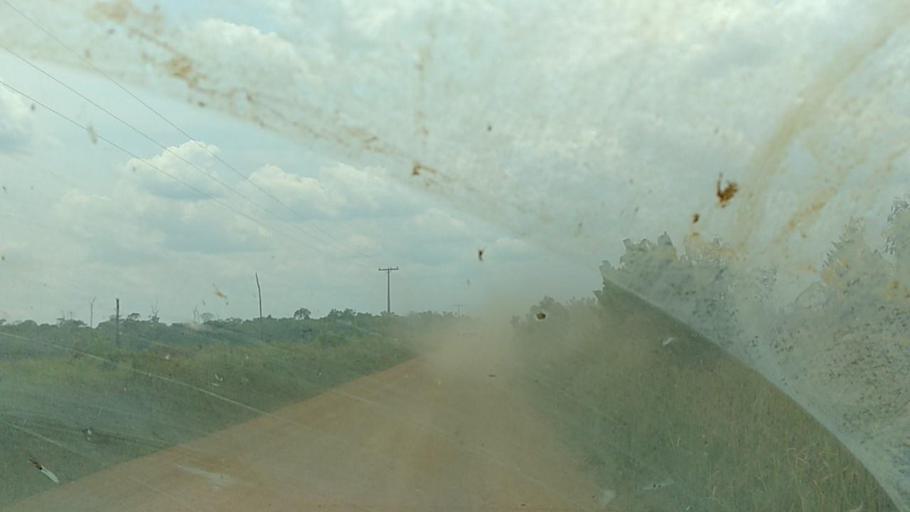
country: BR
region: Rondonia
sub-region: Porto Velho
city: Porto Velho
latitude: -8.9515
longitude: -64.3162
